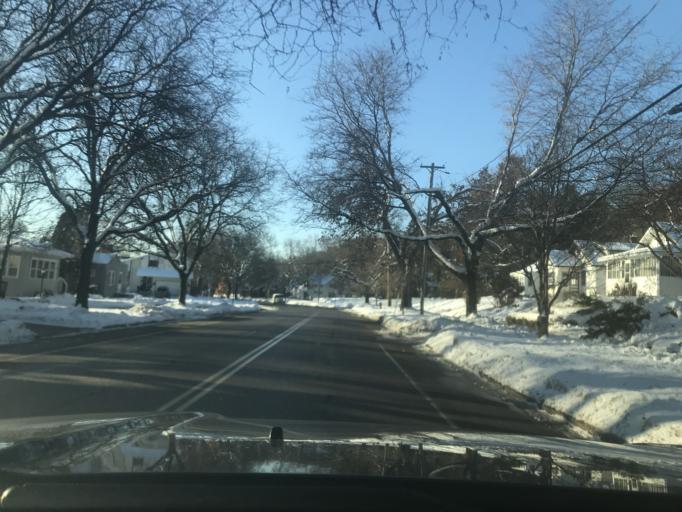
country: US
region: Minnesota
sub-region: Dakota County
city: Mendota Heights
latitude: 44.9186
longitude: -93.1474
